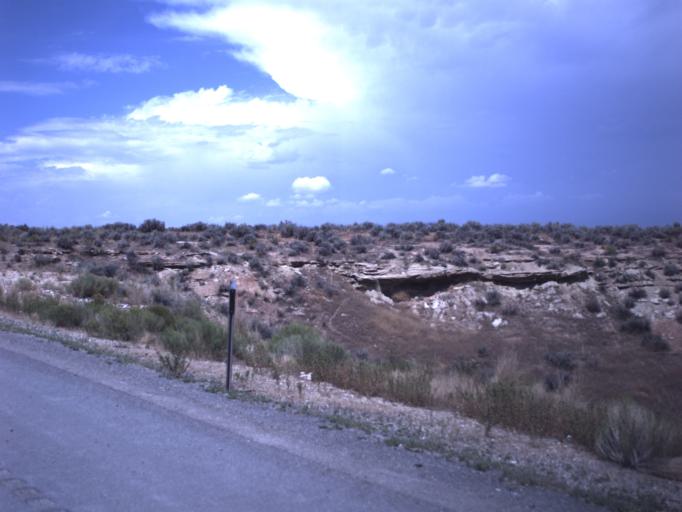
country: US
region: Utah
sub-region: Uintah County
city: Maeser
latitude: 40.3138
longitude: -109.7142
